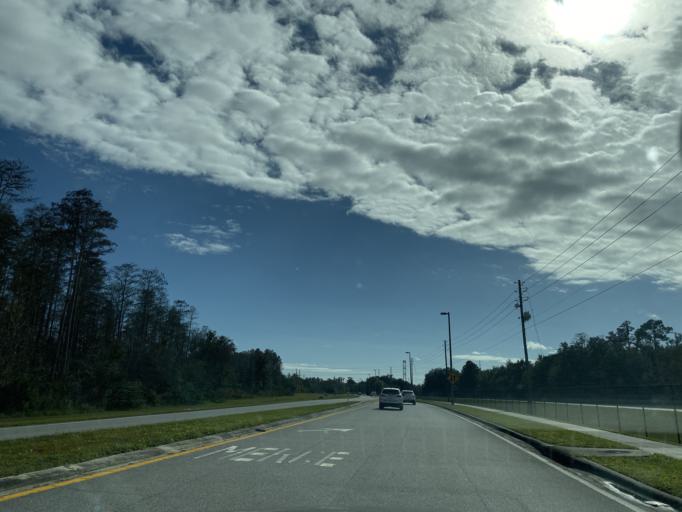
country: US
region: Florida
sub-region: Orange County
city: Azalea Park
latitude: 28.5070
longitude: -81.2565
